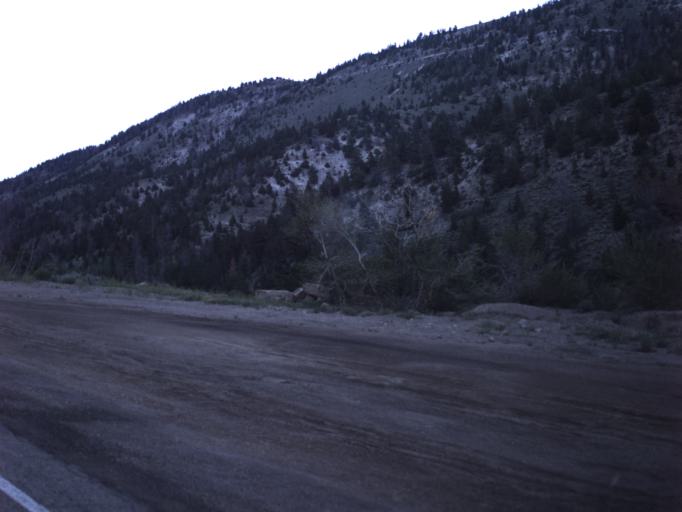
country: US
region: Utah
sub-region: Carbon County
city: Helper
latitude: 39.8511
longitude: -110.7659
